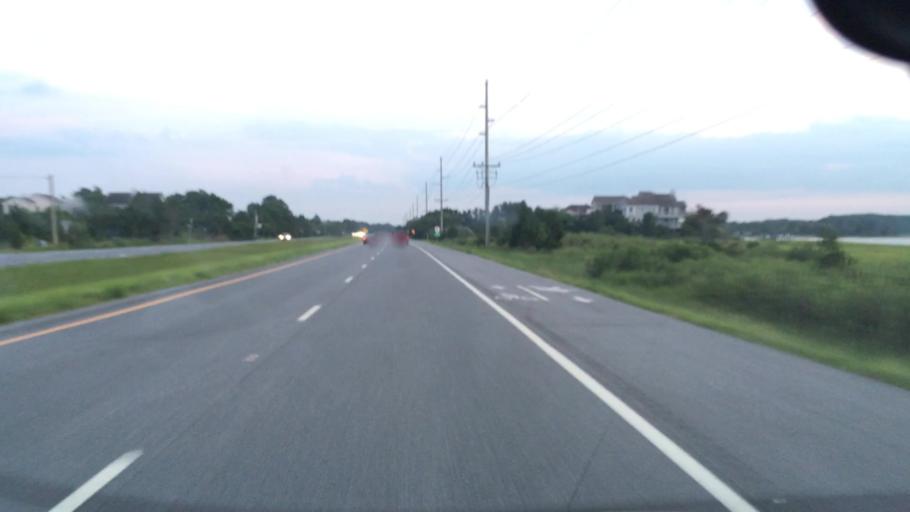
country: US
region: Delaware
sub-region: Sussex County
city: Bethany Beach
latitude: 38.5863
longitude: -75.0620
